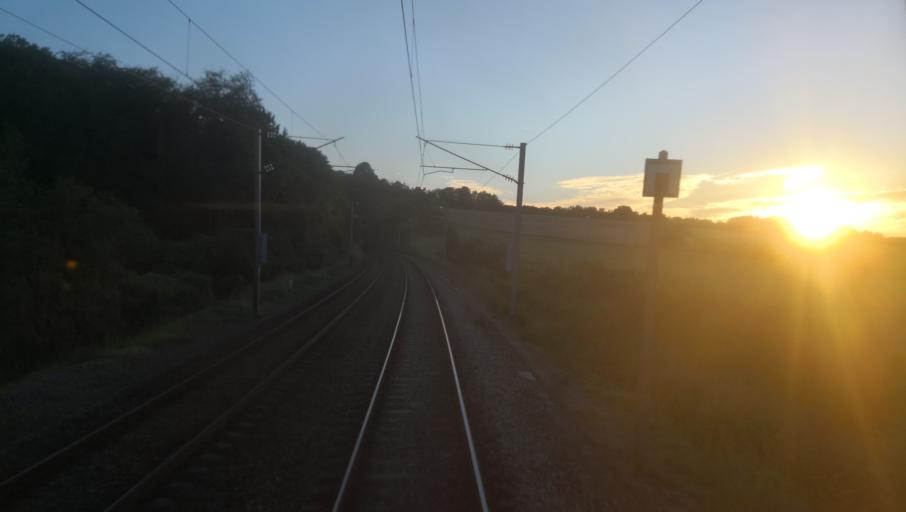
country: FR
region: Haute-Normandie
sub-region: Departement de l'Eure
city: Menilles
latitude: 48.9945
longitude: 1.3023
